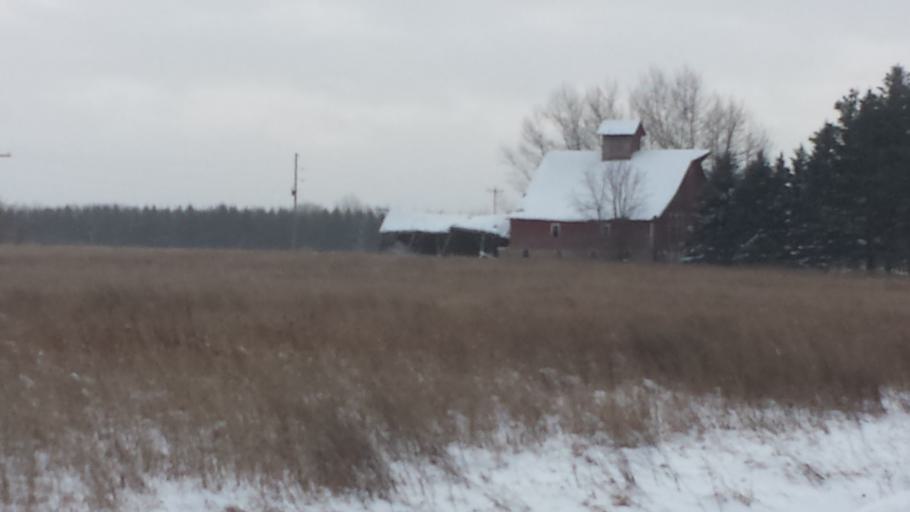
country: US
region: Michigan
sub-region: Montcalm County
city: Lakeview
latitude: 43.4943
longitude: -85.2841
